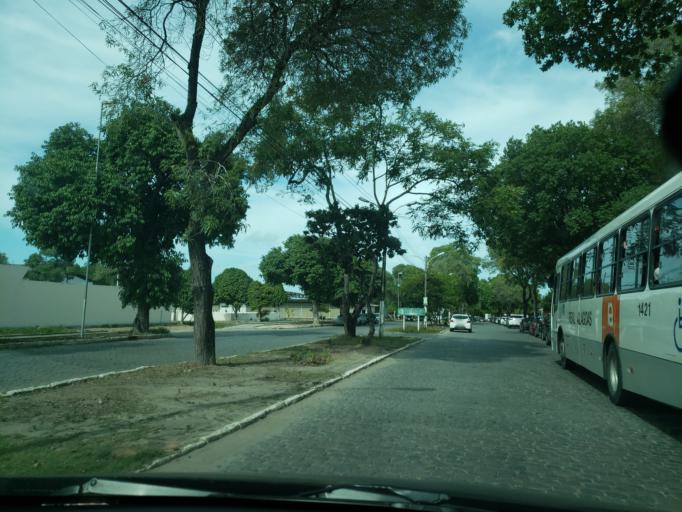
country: BR
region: Alagoas
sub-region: Satuba
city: Satuba
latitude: -9.5566
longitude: -35.7797
